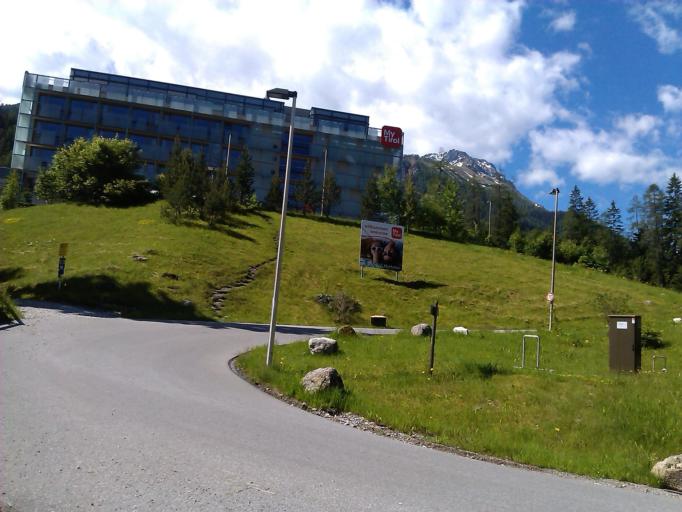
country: AT
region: Tyrol
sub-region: Politischer Bezirk Reutte
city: Biberwier
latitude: 47.3725
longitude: 10.8884
